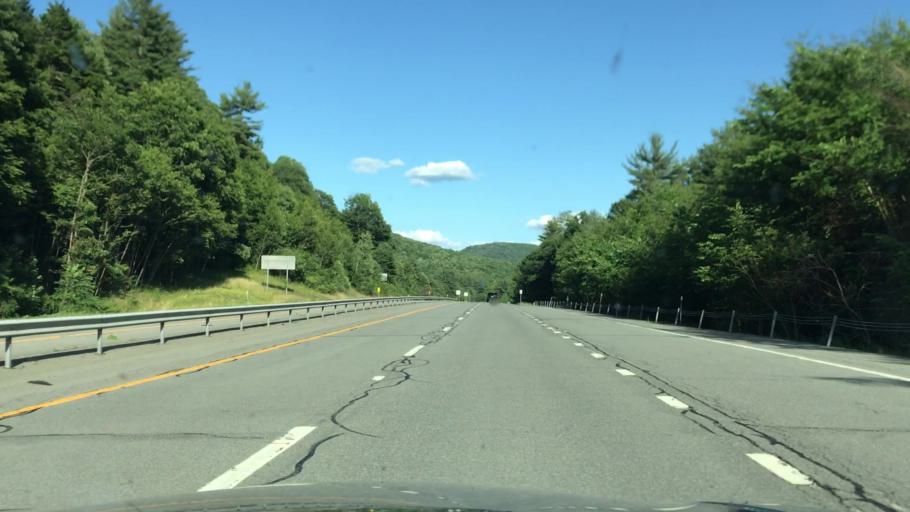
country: US
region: New York
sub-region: Delaware County
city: Hancock
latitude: 41.9886
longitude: -75.1239
